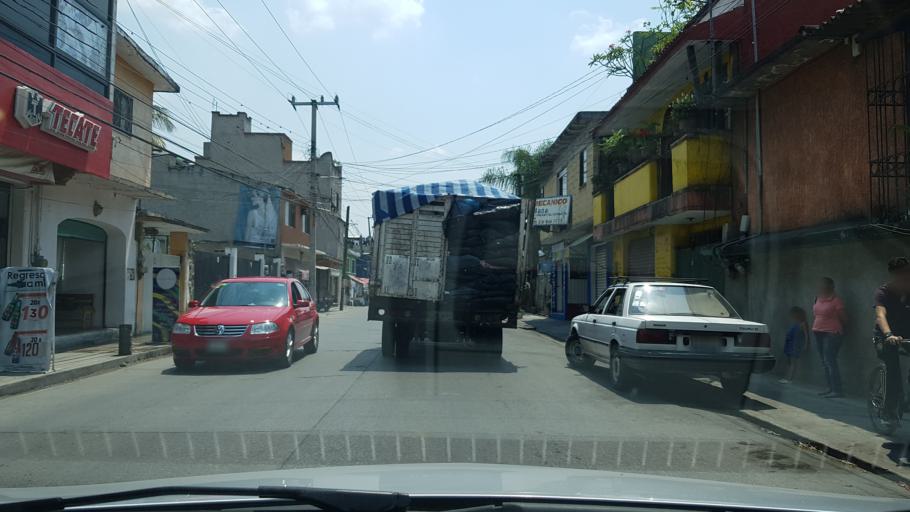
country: MX
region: Morelos
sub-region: Jiutepec
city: Jiutepec
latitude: 18.8778
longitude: -99.1754
